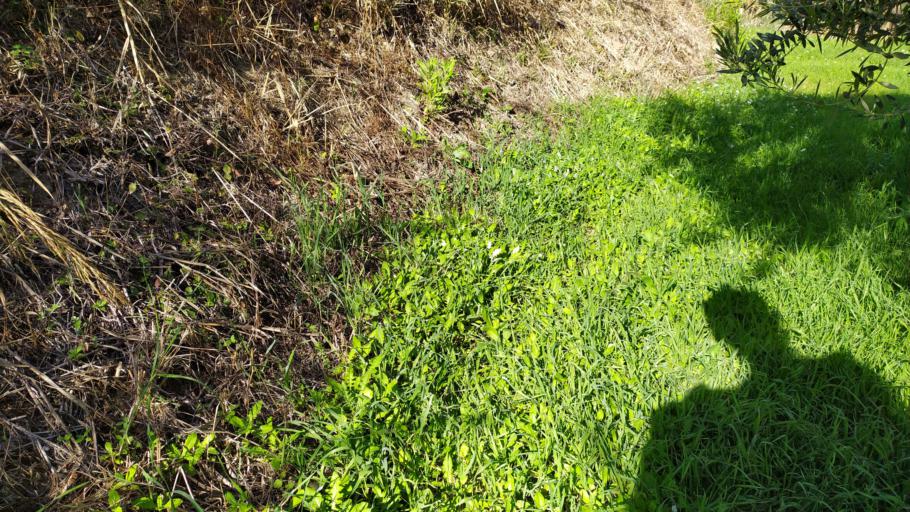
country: IT
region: Sicily
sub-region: Messina
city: Gualtieri Sicamino
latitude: 38.1603
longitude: 15.2981
